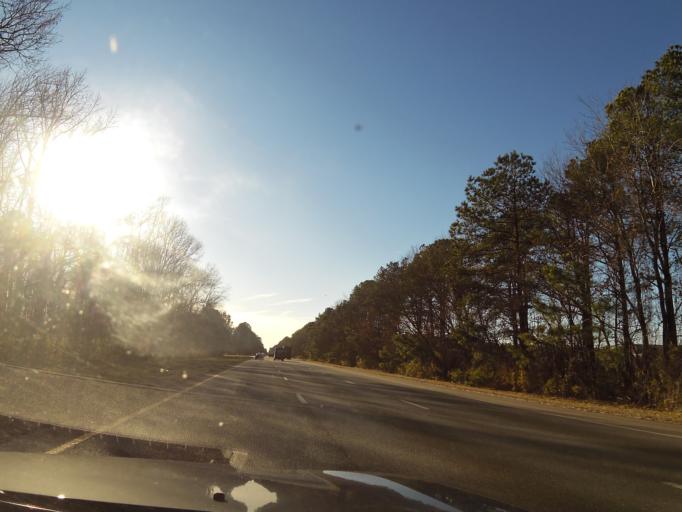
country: US
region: Virginia
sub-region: City of Portsmouth
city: Portsmouth Heights
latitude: 36.7734
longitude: -76.4552
